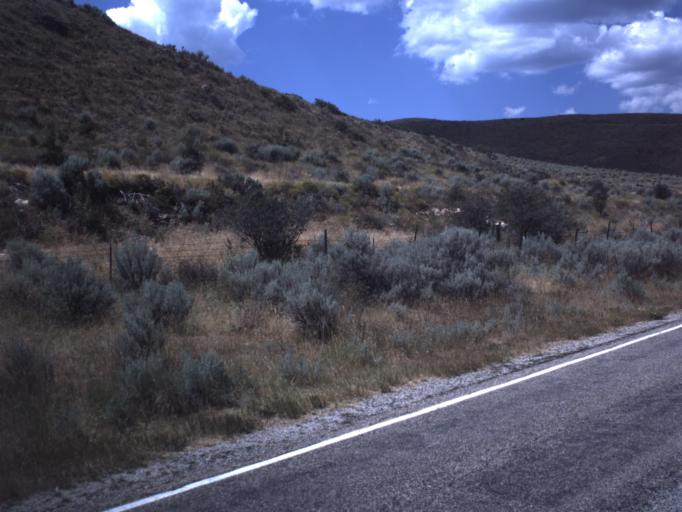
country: US
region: Utah
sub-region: Rich County
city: Randolph
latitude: 41.8505
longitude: -111.3576
